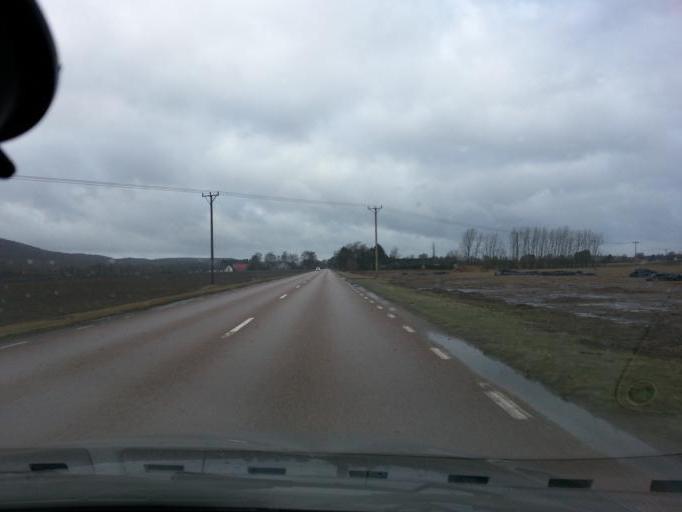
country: SE
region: Skane
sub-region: Klippans Kommun
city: Klippan
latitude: 56.0907
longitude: 13.1615
